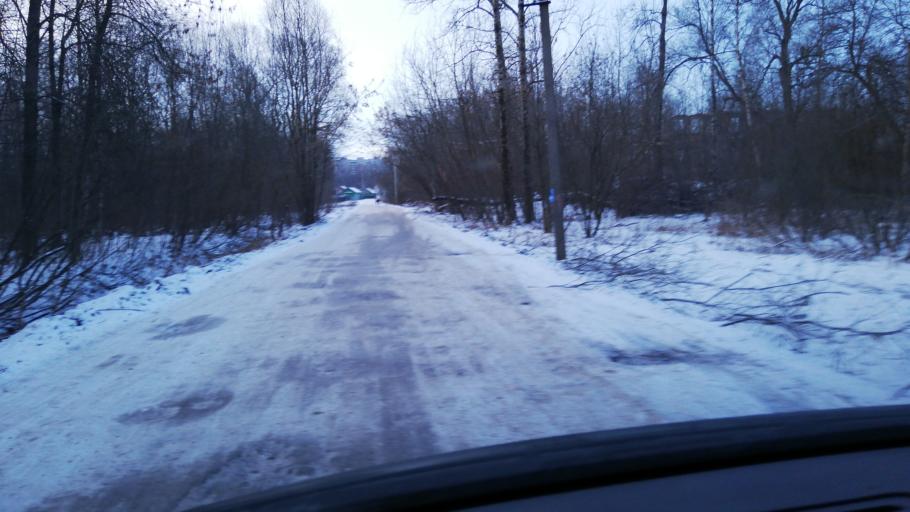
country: RU
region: Jaroslavl
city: Yaroslavl
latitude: 57.5986
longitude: 39.8424
